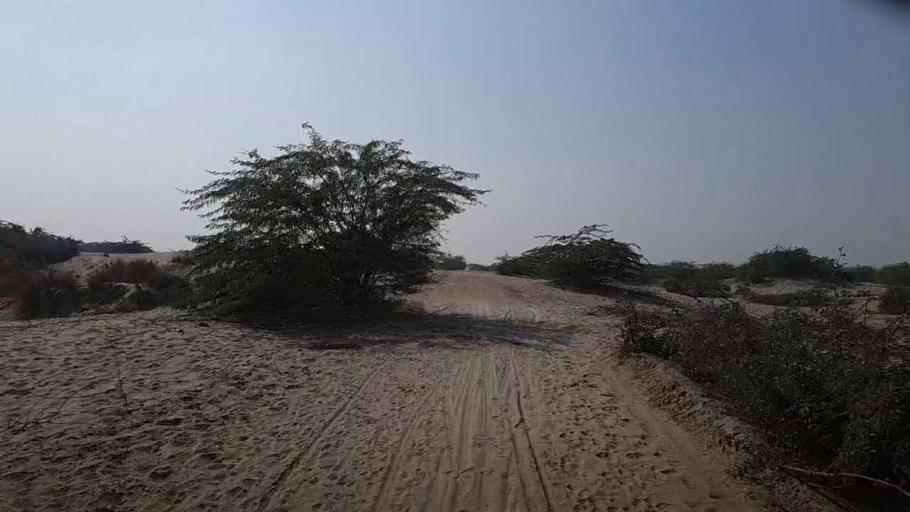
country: PK
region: Sindh
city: Bozdar
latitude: 27.2343
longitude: 68.5959
